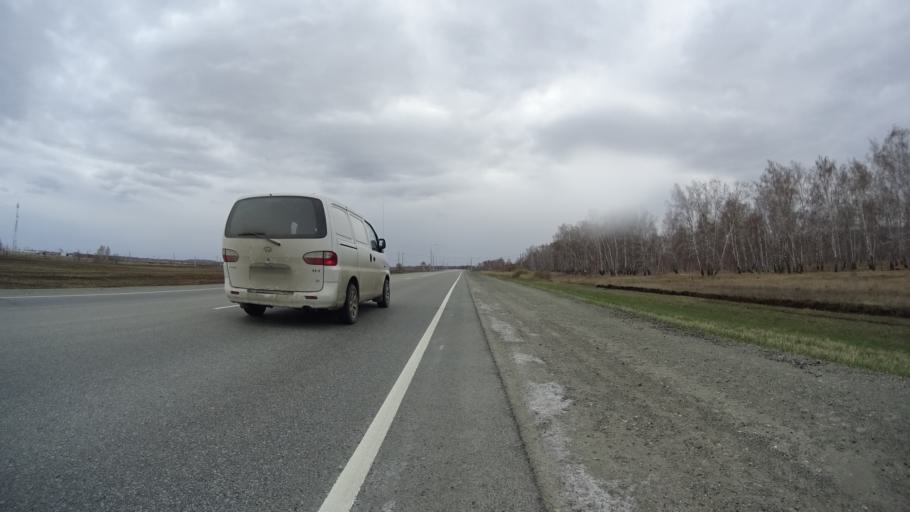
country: RU
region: Chelyabinsk
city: Krasnogorskiy
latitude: 54.6874
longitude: 61.2480
